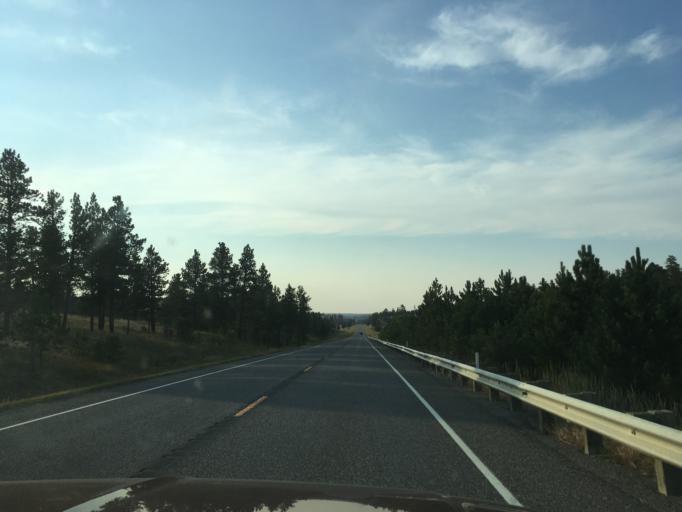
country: US
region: Montana
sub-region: Musselshell County
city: Roundup
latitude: 46.2649
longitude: -108.4682
